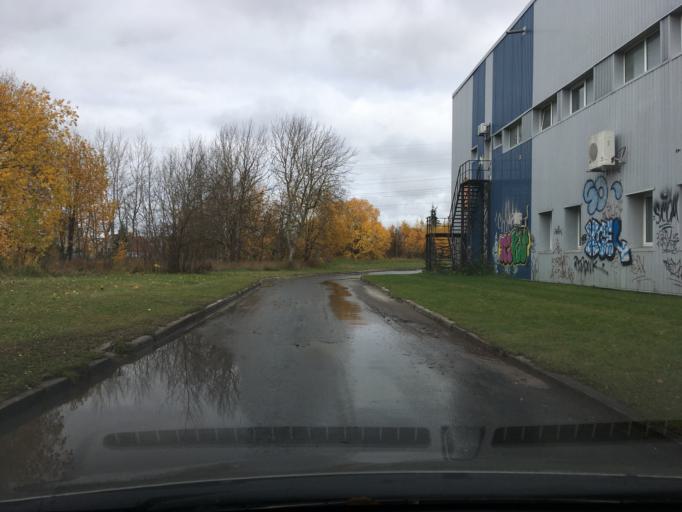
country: EE
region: Harju
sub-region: Tallinna linn
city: Tallinn
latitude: 59.3962
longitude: 24.7215
